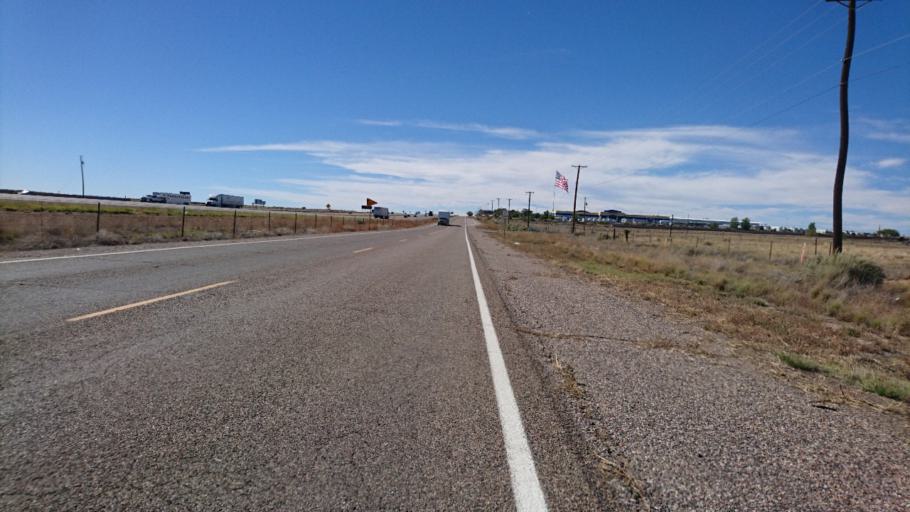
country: US
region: New Mexico
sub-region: Bernalillo County
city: South Valley
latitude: 35.0609
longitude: -106.8015
